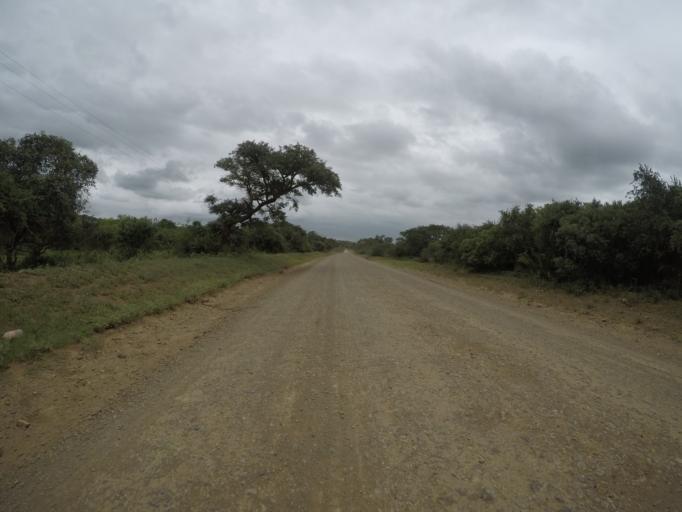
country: ZA
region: KwaZulu-Natal
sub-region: uThungulu District Municipality
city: Empangeni
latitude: -28.5880
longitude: 31.8443
